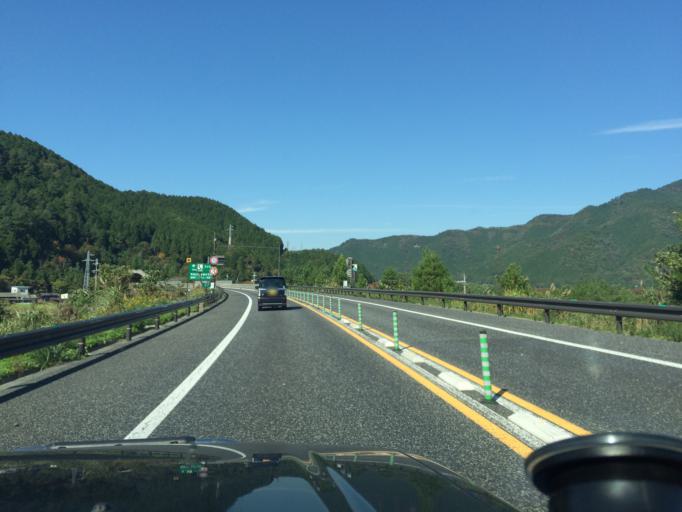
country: JP
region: Kyoto
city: Fukuchiyama
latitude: 35.2243
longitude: 135.0325
